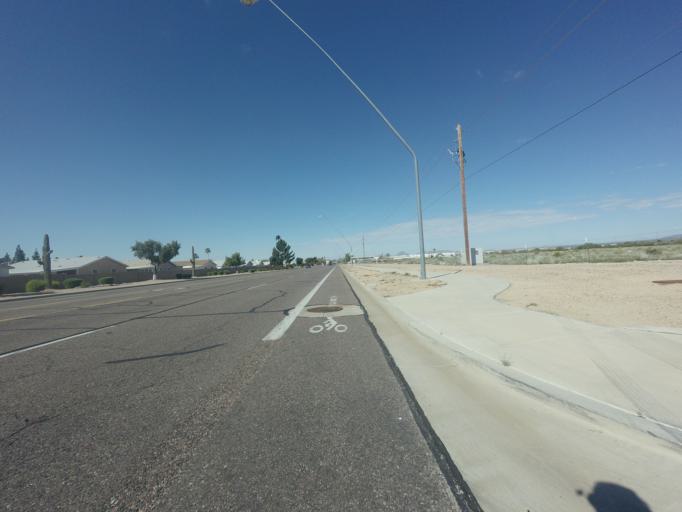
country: US
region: Arizona
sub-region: Maricopa County
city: Mesa
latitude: 33.4664
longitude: -111.7060
